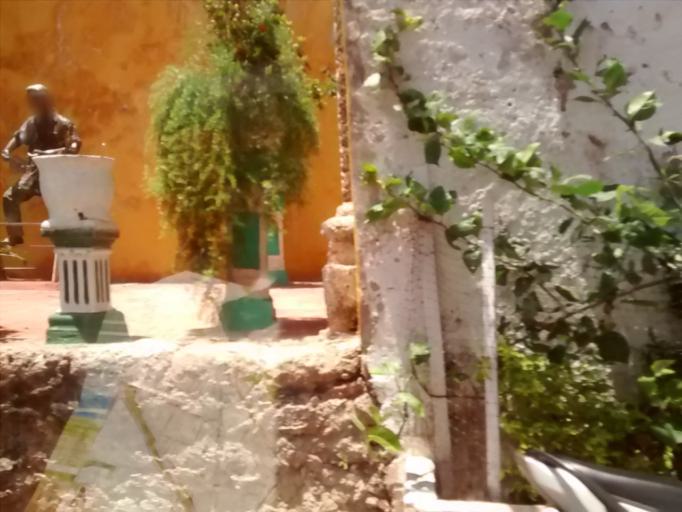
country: CO
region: Bolivar
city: Cartagena
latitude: 10.4204
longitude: -75.5456
